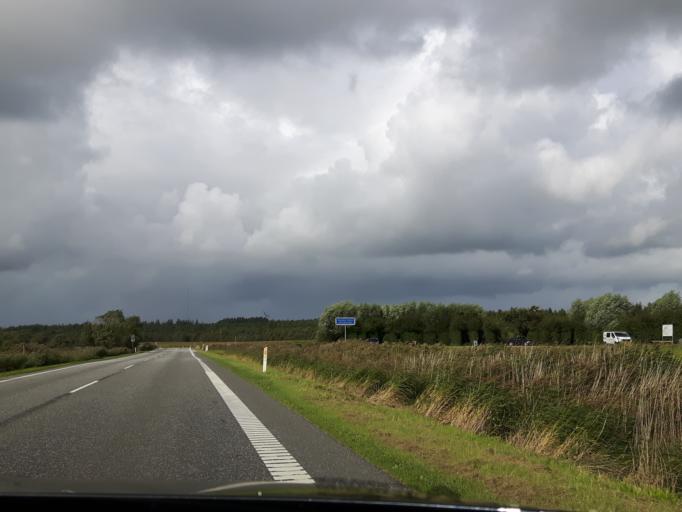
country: DK
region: North Denmark
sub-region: Thisted Kommune
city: Thisted
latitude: 57.0360
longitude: 8.9338
